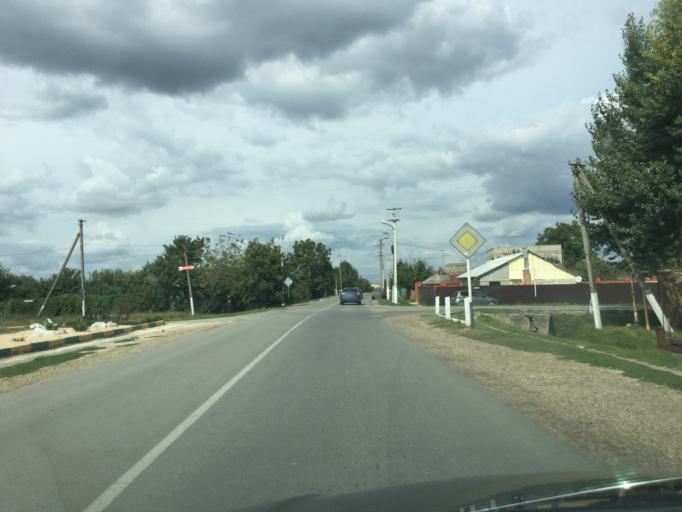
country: RU
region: Krasnodarskiy
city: Sovkhoznyy
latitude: 45.2717
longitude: 38.0993
